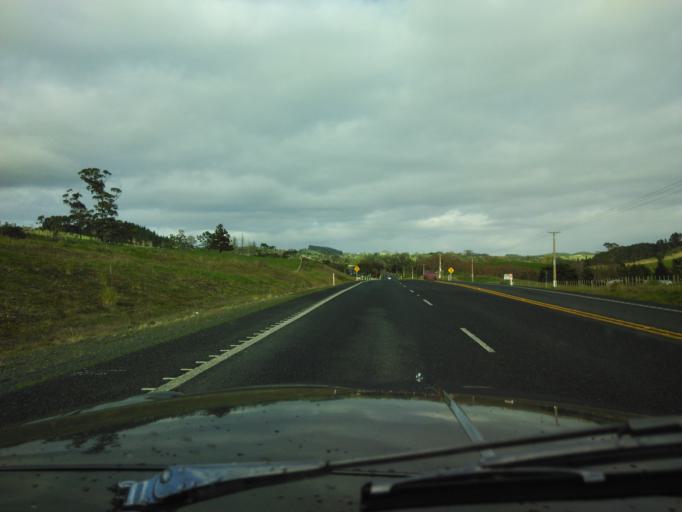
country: NZ
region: Auckland
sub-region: Auckland
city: Wellsford
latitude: -36.2417
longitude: 174.5105
